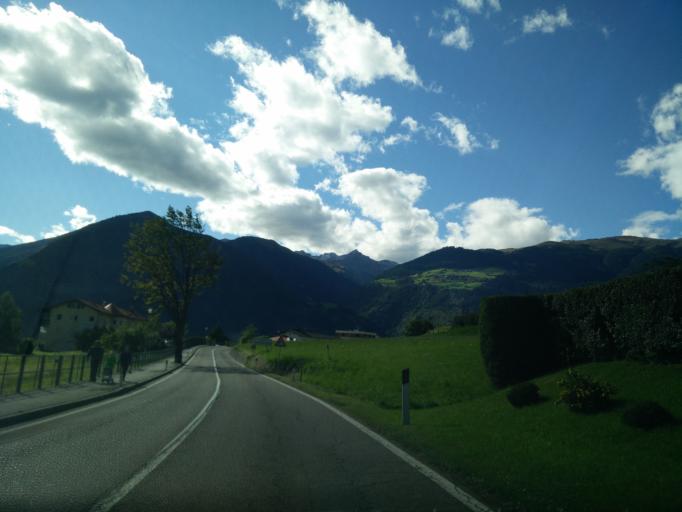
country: IT
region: Trentino-Alto Adige
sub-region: Bolzano
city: Malles Venosta
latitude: 46.6845
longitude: 10.5571
